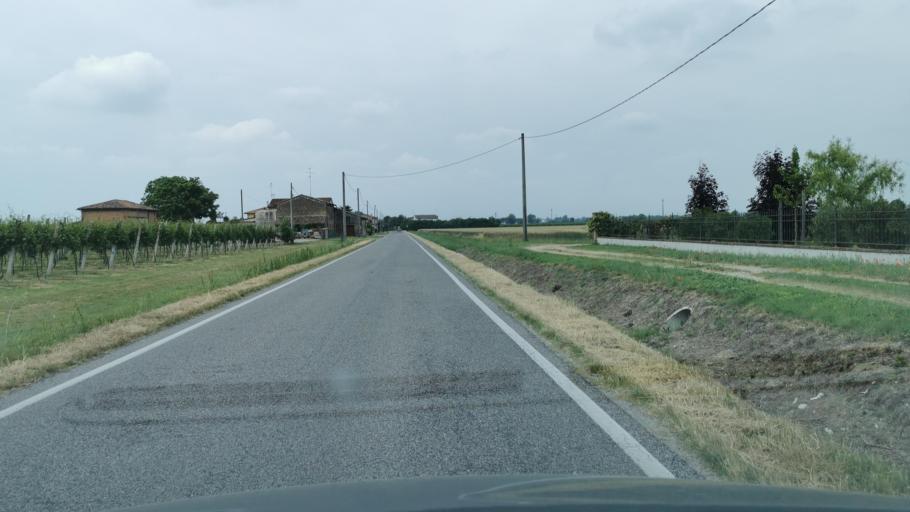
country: IT
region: Emilia-Romagna
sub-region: Provincia di Ravenna
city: Villanova
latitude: 44.4321
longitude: 12.0293
